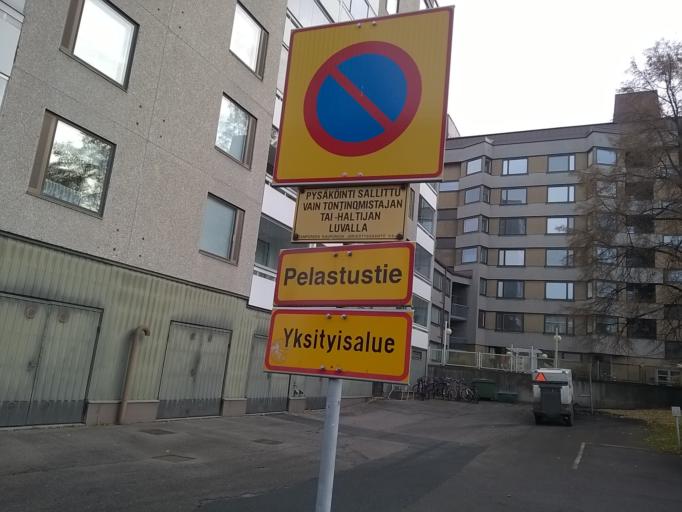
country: FI
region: Pirkanmaa
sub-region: Tampere
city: Tampere
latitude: 61.5001
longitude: 23.7780
